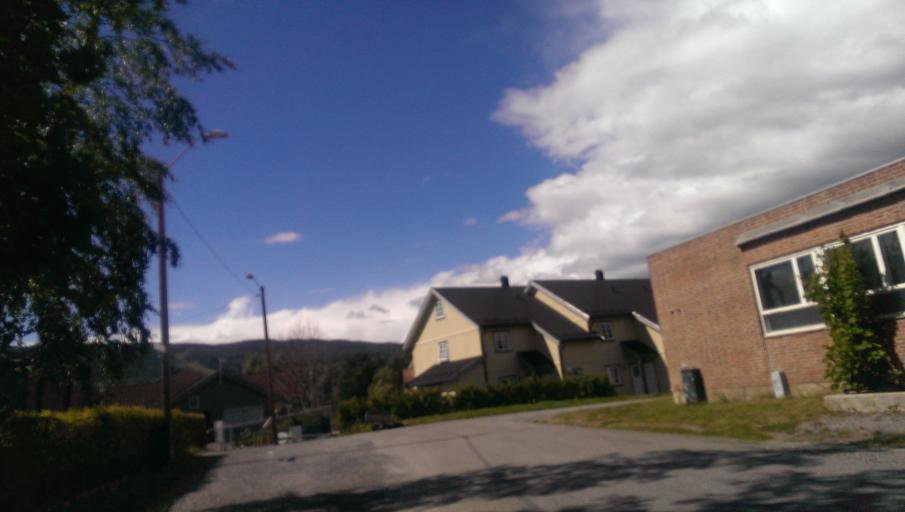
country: NO
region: Buskerud
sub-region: Kongsberg
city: Kongsberg
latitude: 59.6577
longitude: 9.6554
